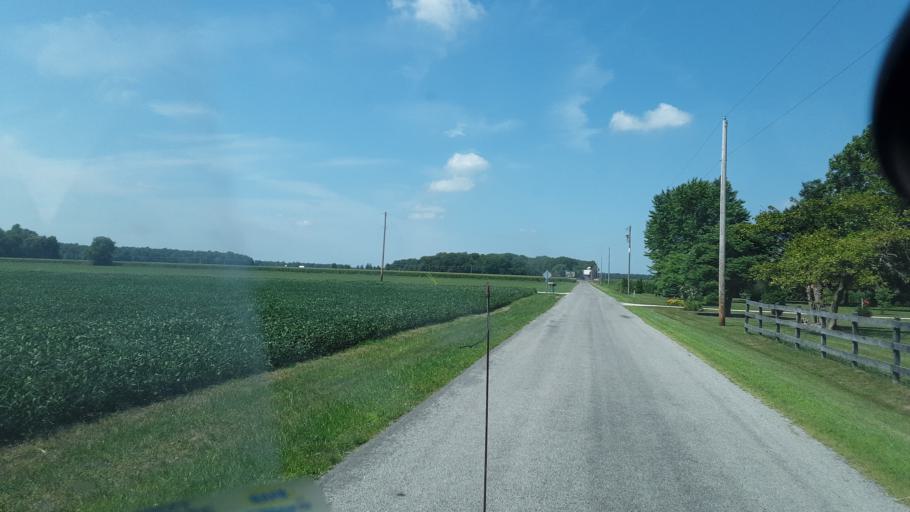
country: US
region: Ohio
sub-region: Hancock County
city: Findlay
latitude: 40.9746
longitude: -83.5464
